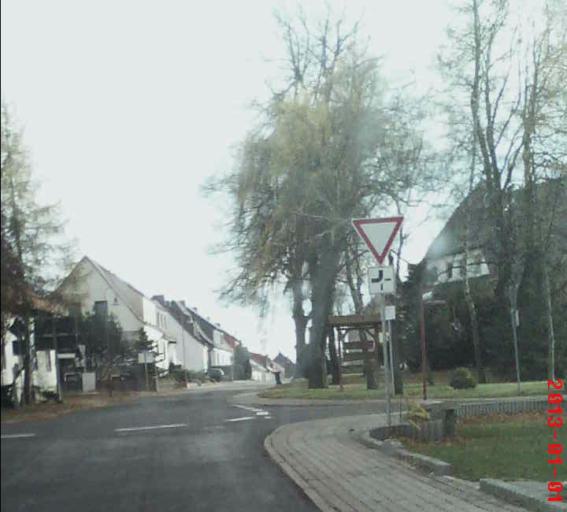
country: DE
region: Thuringia
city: Wachstedt
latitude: 51.2949
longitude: 10.2461
